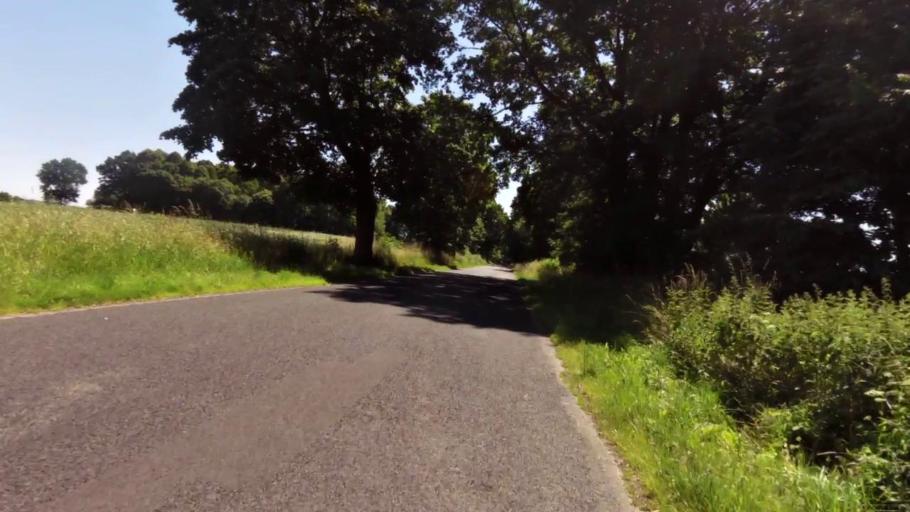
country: PL
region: West Pomeranian Voivodeship
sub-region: Powiat swidwinski
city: Rabino
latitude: 53.8475
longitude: 15.9901
